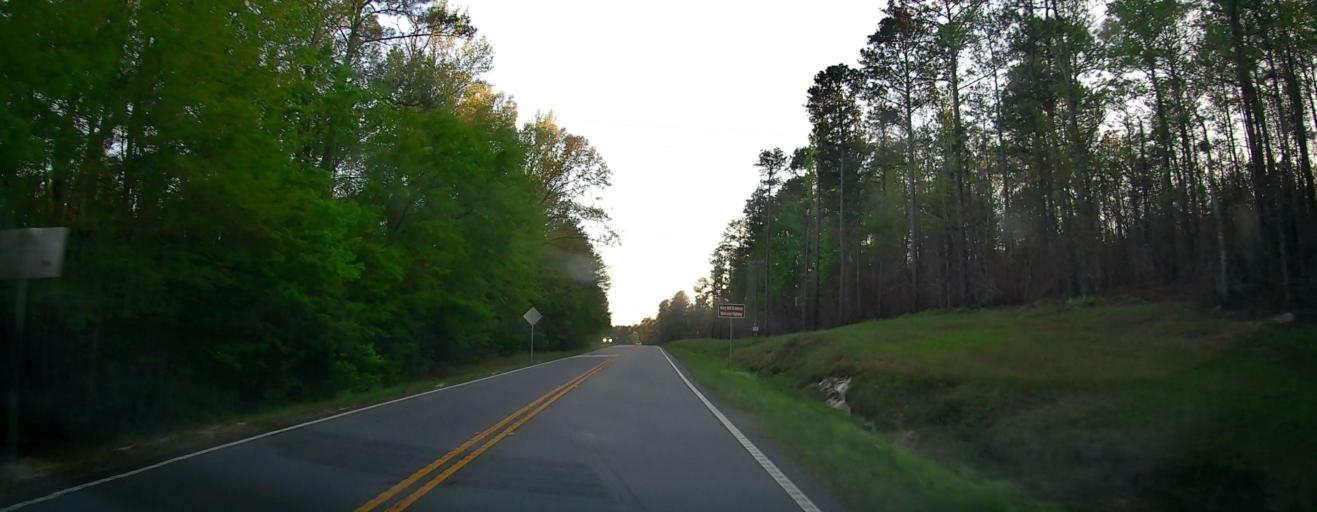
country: US
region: Georgia
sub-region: Talbot County
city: Talbotton
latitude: 32.5202
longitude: -84.6040
